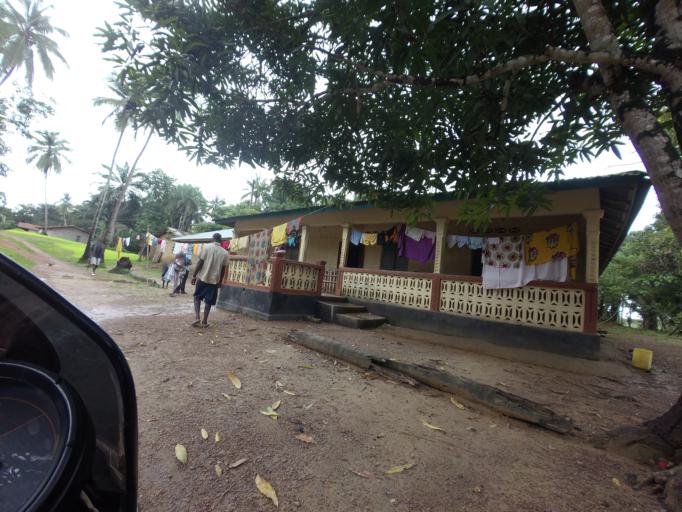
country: SL
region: Northern Province
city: Mambolo
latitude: 8.9686
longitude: -13.0021
